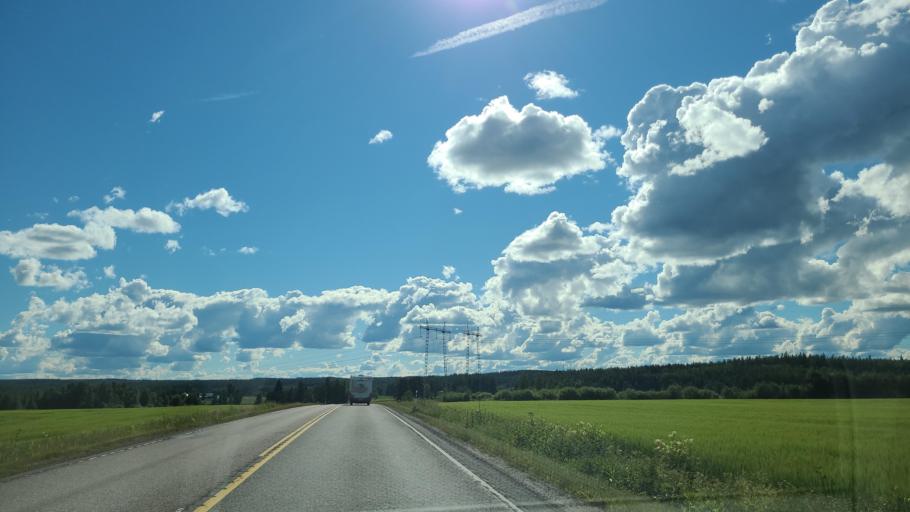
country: FI
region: Central Finland
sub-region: Jaemsae
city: Jaemsae
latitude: 61.8435
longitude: 25.1395
